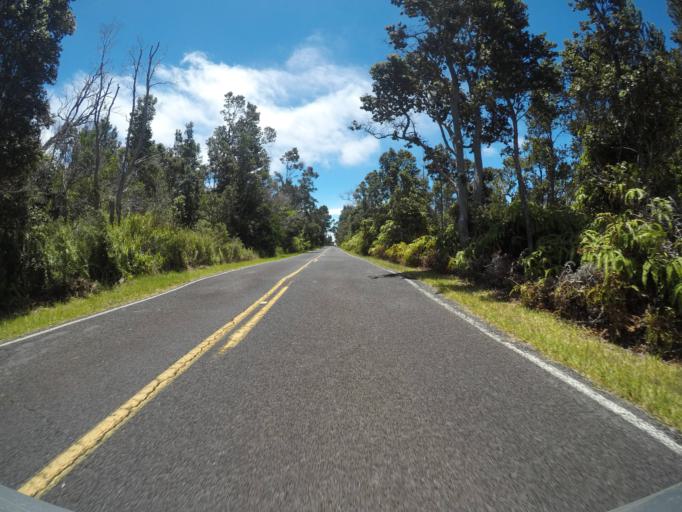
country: US
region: Hawaii
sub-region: Hawaii County
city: Volcano
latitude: 19.3657
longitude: -155.2182
